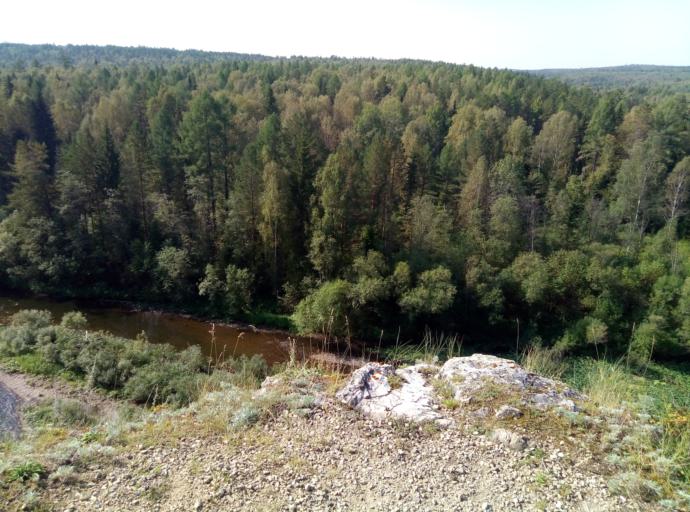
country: RU
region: Sverdlovsk
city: Krasnotur'insk
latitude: 59.6511
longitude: 60.1794
